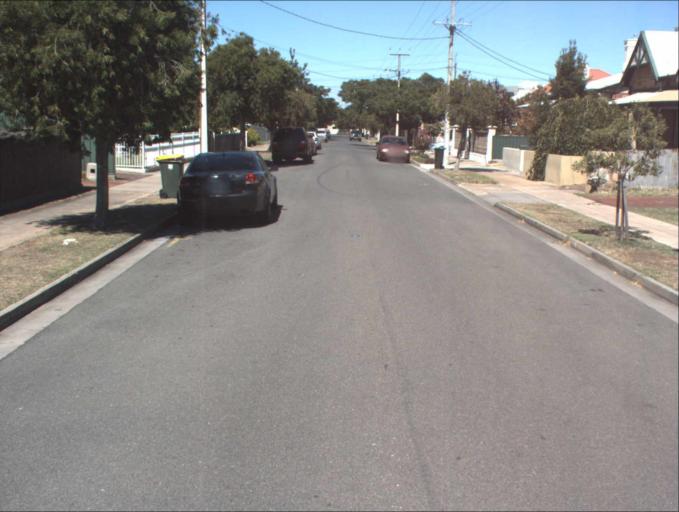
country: AU
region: South Australia
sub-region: Port Adelaide Enfield
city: Birkenhead
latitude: -34.8316
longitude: 138.4844
